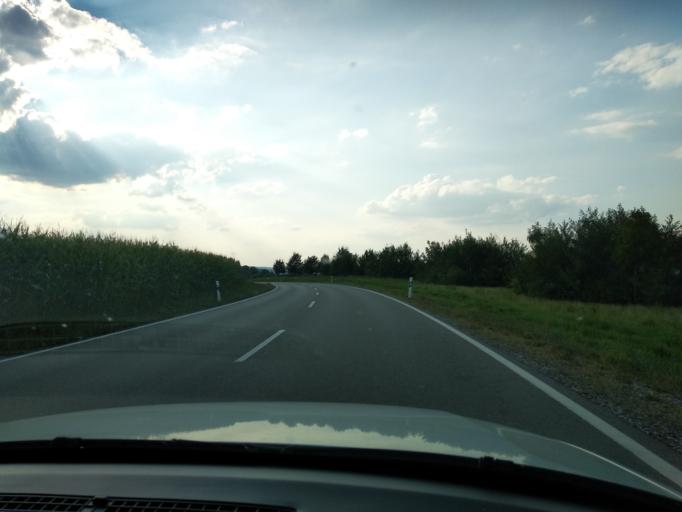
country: DE
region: Bavaria
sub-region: Swabia
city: Trunkelsberg
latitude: 47.9970
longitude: 10.2160
